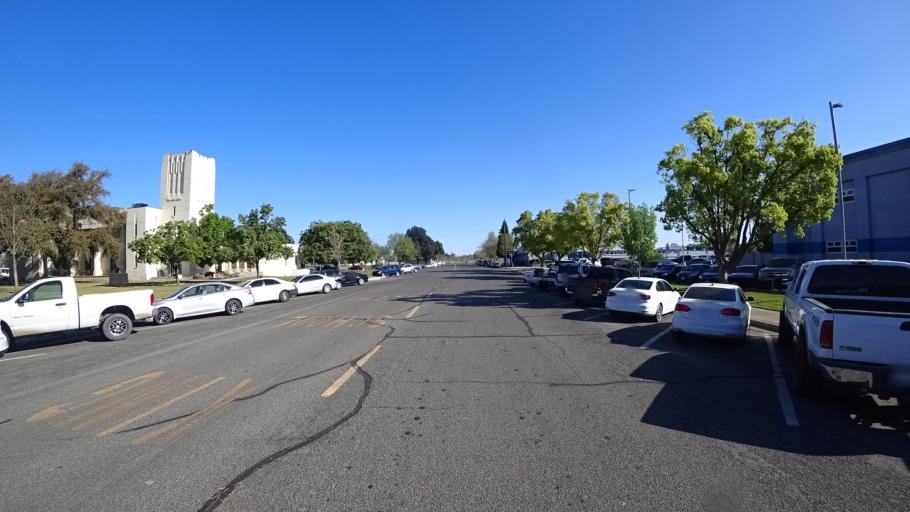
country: US
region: California
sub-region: Glenn County
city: Orland
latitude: 39.7512
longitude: -122.1928
